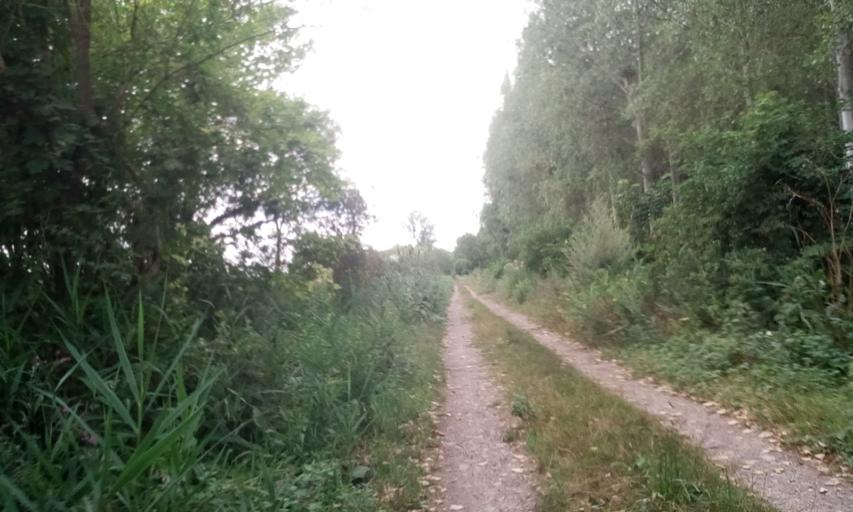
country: FR
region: Lower Normandy
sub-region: Departement du Calvados
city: Argences
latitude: 49.1462
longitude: -0.1810
